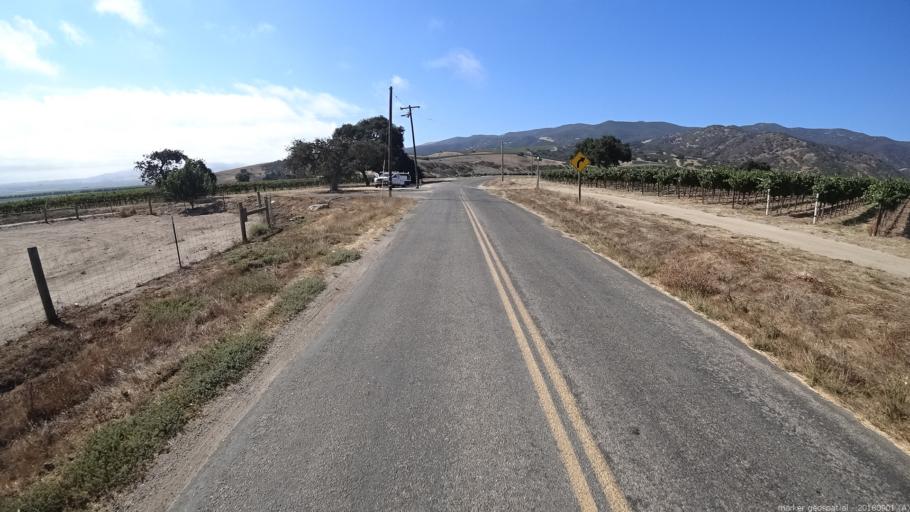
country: US
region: California
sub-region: Monterey County
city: Soledad
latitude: 36.3404
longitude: -121.3425
